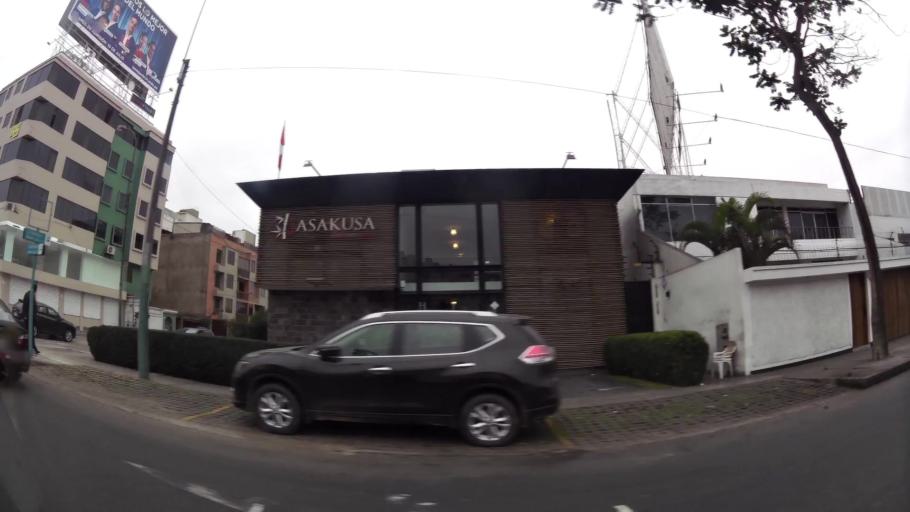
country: PE
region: Lima
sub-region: Lima
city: San Luis
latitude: -12.0870
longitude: -76.9940
